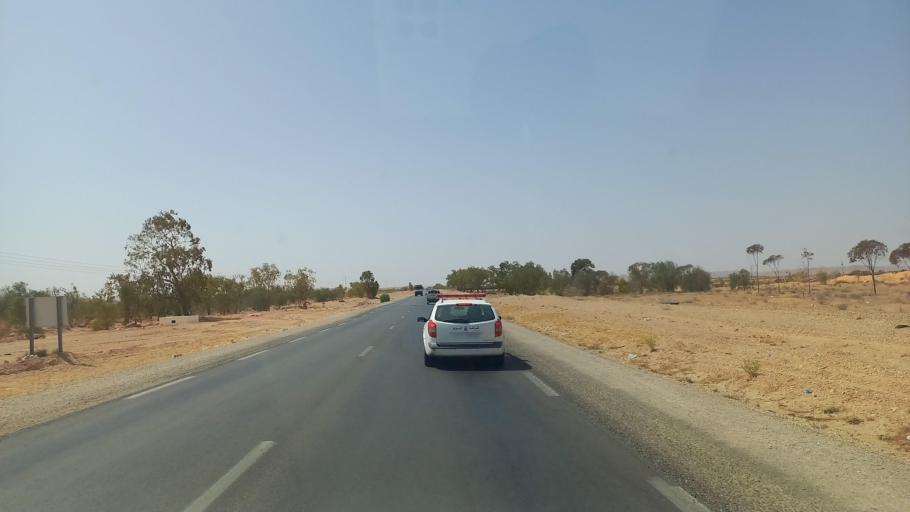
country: TN
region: Madanin
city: Medenine
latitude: 33.2237
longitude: 10.4507
